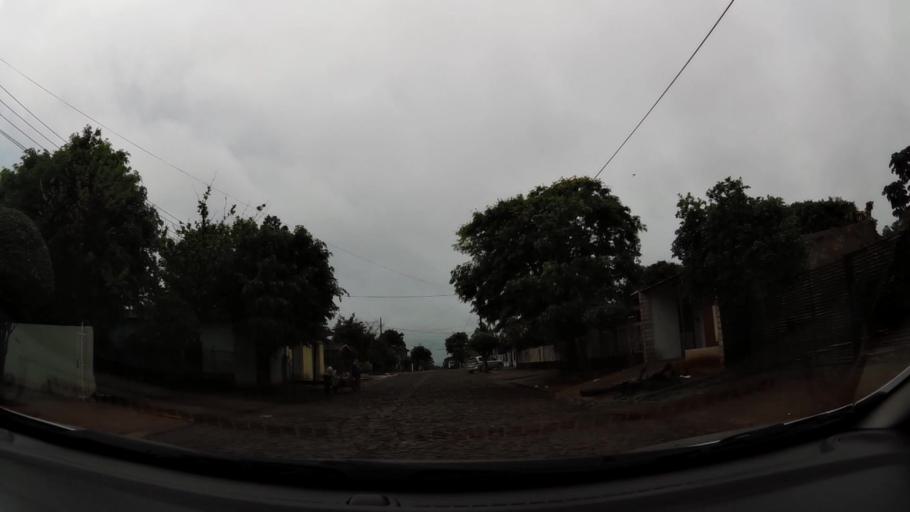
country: PY
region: Alto Parana
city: Presidente Franco
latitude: -25.5144
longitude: -54.6708
